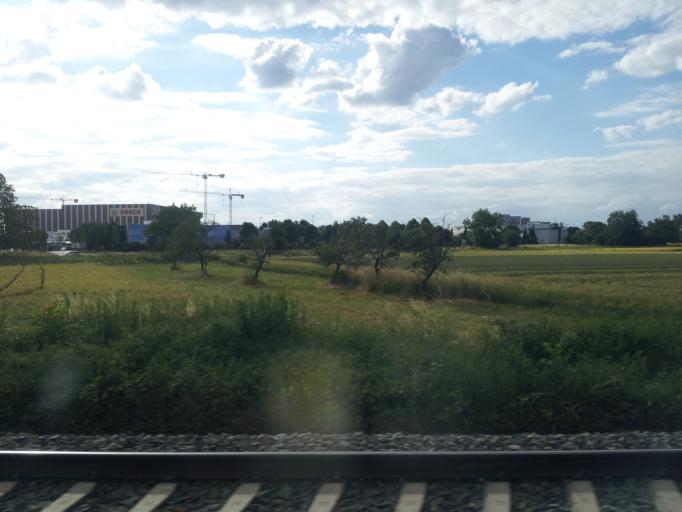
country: DE
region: Baden-Wuerttemberg
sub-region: Karlsruhe Region
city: Weingarten
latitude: 49.0176
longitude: 8.4819
